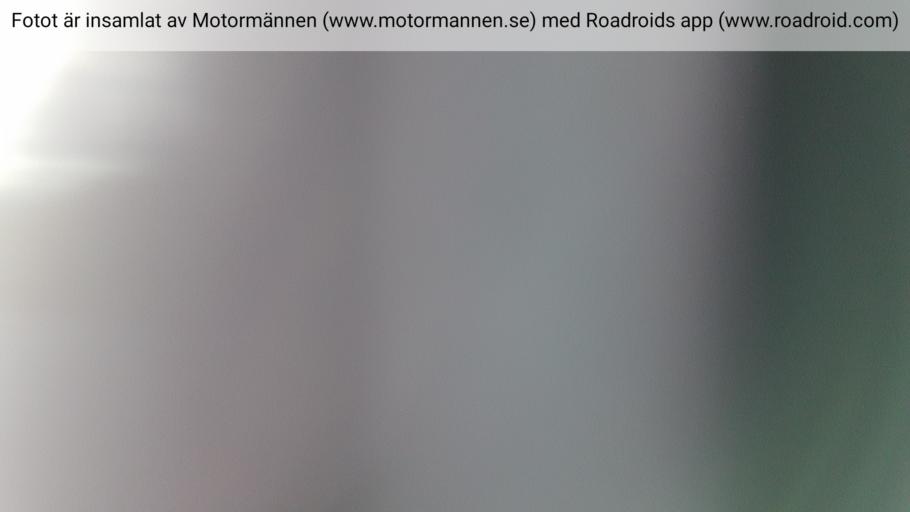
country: SE
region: Vaestra Goetaland
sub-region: Skovde Kommun
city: Skoevde
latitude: 58.4136
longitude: 13.8812
